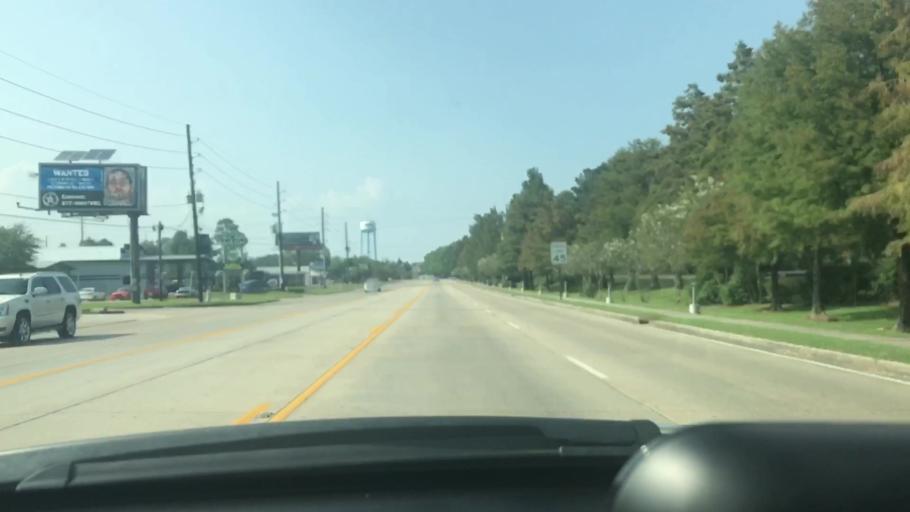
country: US
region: Louisiana
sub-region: Tangipahoa Parish
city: Hammond
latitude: 30.4941
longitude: -90.4583
